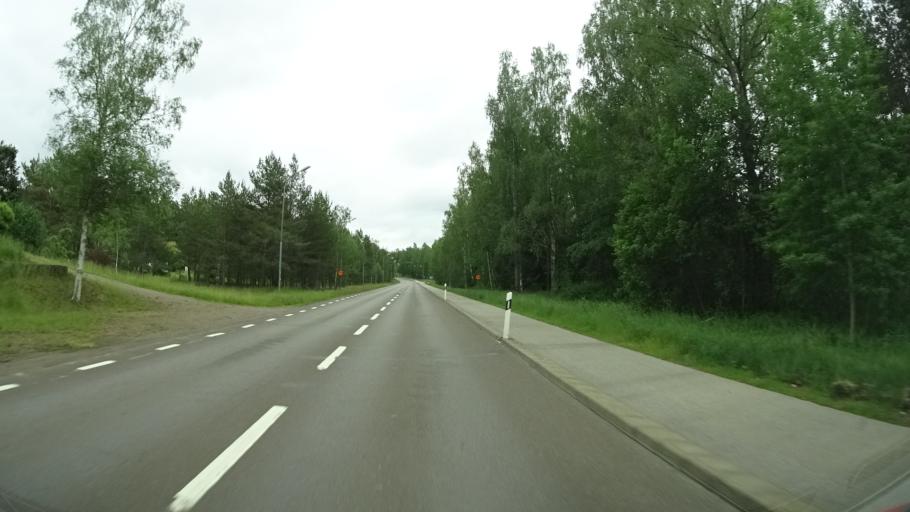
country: SE
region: Kalmar
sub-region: Hultsfreds Kommun
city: Hultsfred
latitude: 57.5504
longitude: 15.7235
